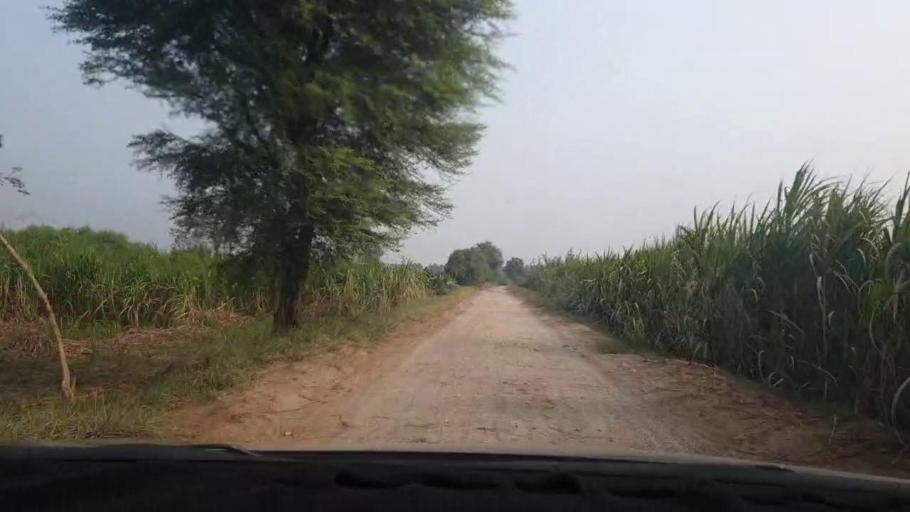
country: PK
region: Sindh
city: Matiari
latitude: 25.5798
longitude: 68.5151
